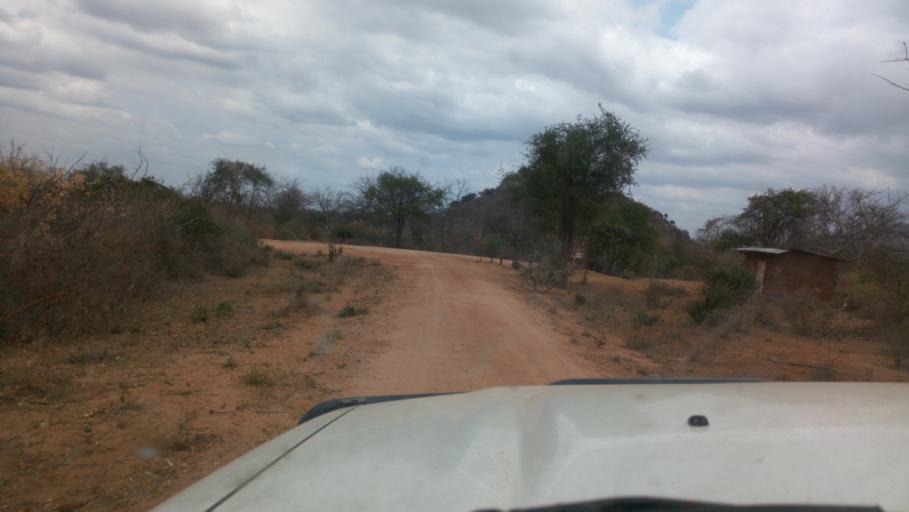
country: KE
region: Kitui
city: Kitui
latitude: -1.8949
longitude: 38.4106
